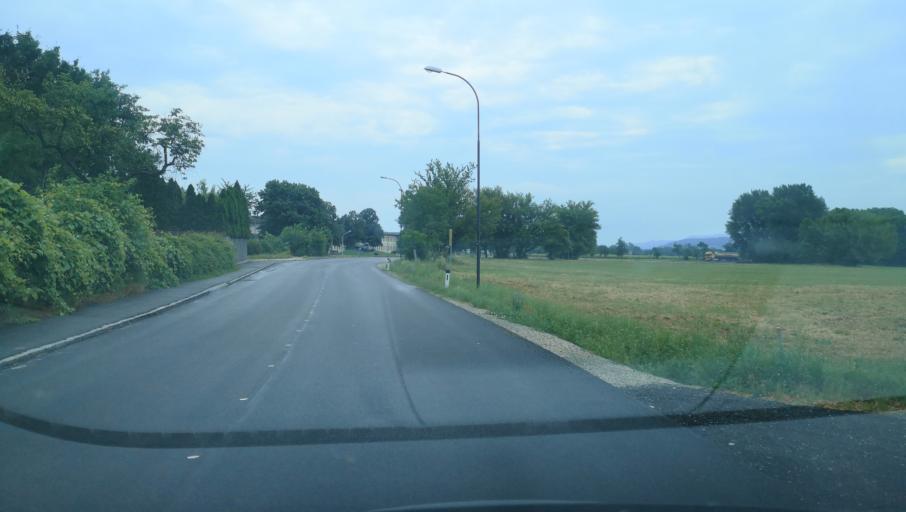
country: AT
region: Lower Austria
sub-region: Politischer Bezirk Krems
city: Weinzierl bei Krems
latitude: 48.3916
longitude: 15.5825
